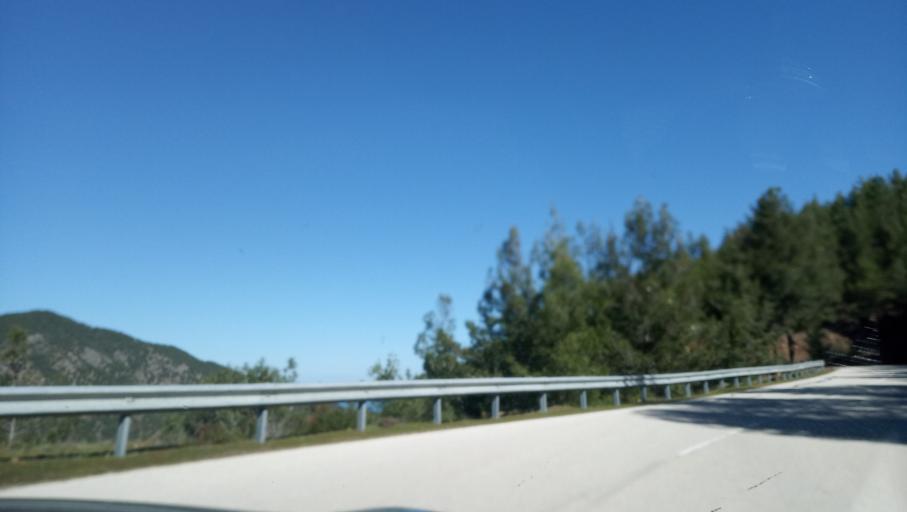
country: CY
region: Lefkosia
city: Lefka
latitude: 35.0683
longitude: 32.7501
